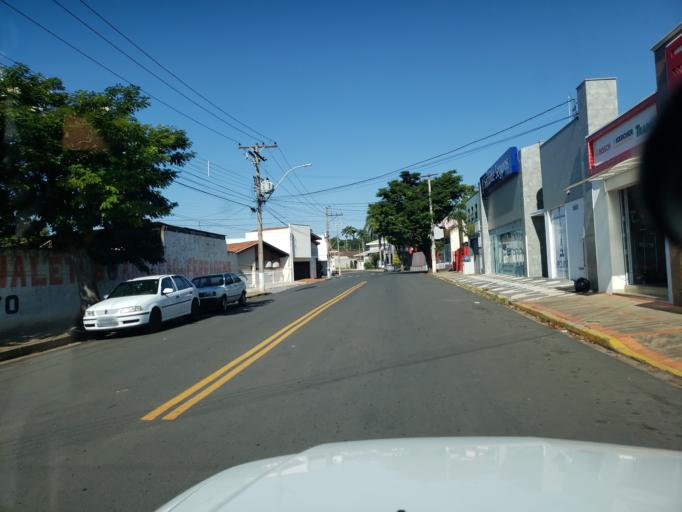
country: BR
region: Sao Paulo
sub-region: Itapira
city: Itapira
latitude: -22.4413
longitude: -46.8318
